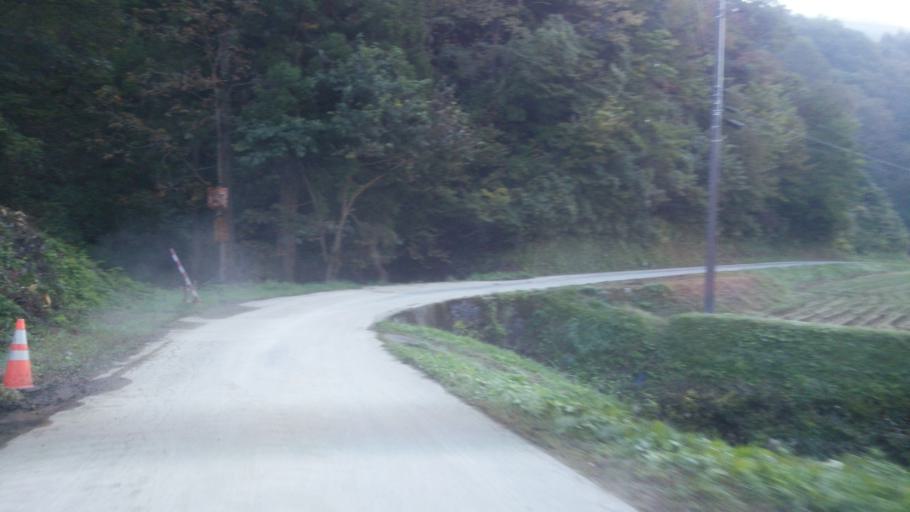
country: JP
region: Fukushima
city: Kitakata
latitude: 37.4098
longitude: 139.7305
